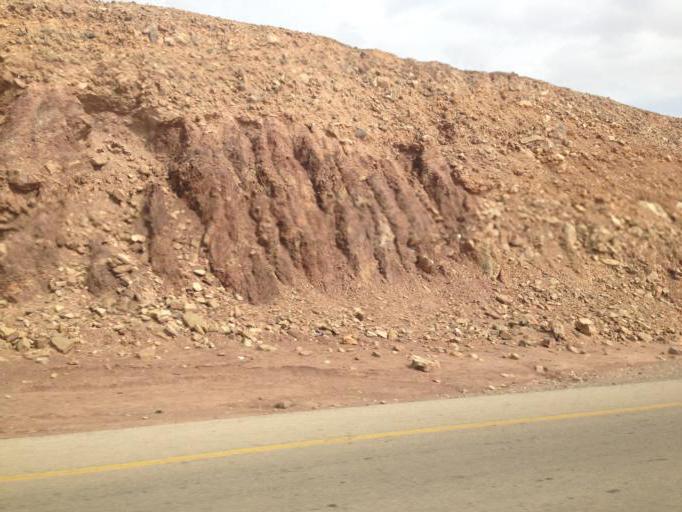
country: OM
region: Ash Sharqiyah
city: Badiyah
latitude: 22.5224
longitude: 58.9498
